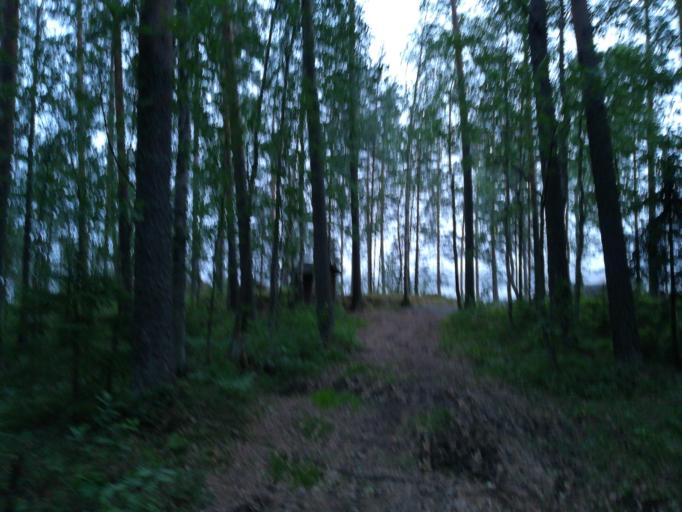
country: FI
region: Southern Savonia
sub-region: Mikkeli
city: Ristiina
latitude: 61.4828
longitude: 27.2861
